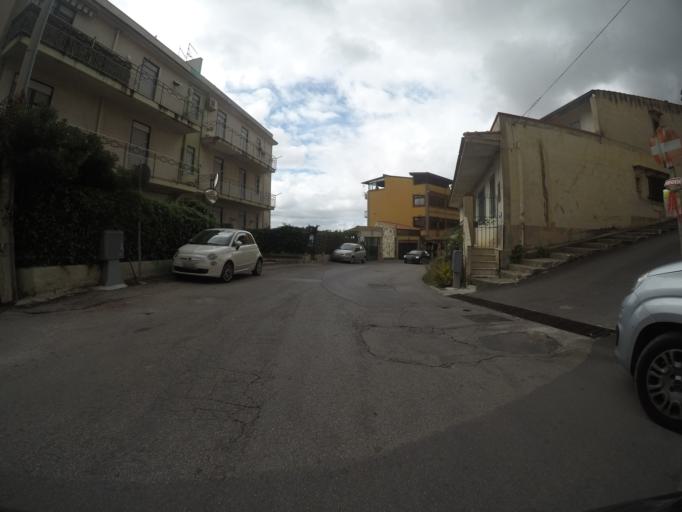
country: IT
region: Sicily
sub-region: Palermo
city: Montelepre
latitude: 38.0923
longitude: 13.1732
